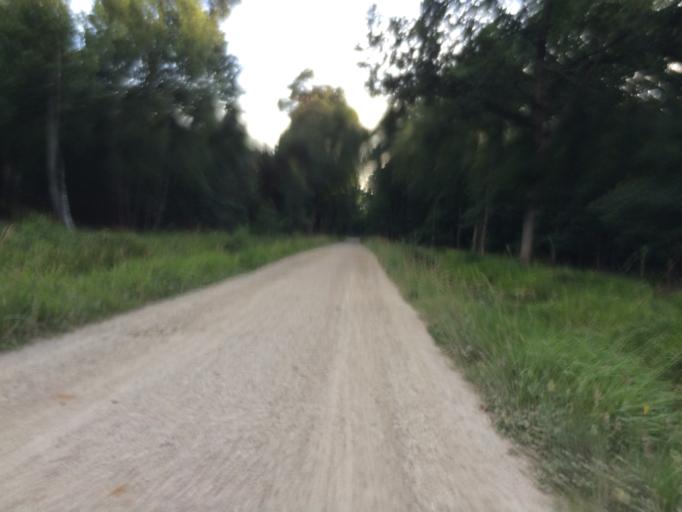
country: FR
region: Ile-de-France
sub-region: Departement de l'Essonne
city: Soisy-sur-Seine
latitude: 48.6651
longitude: 2.4772
